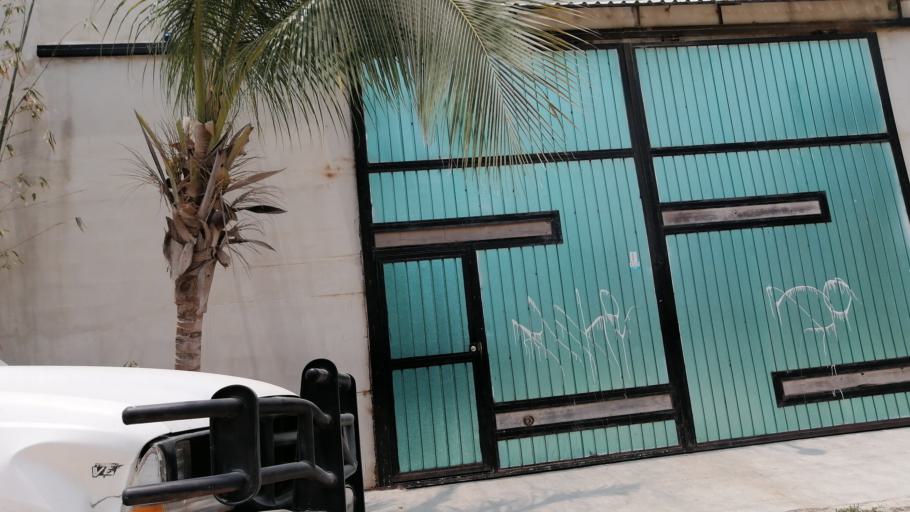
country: MX
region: Quintana Roo
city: Cancun
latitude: 21.1355
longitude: -86.8975
